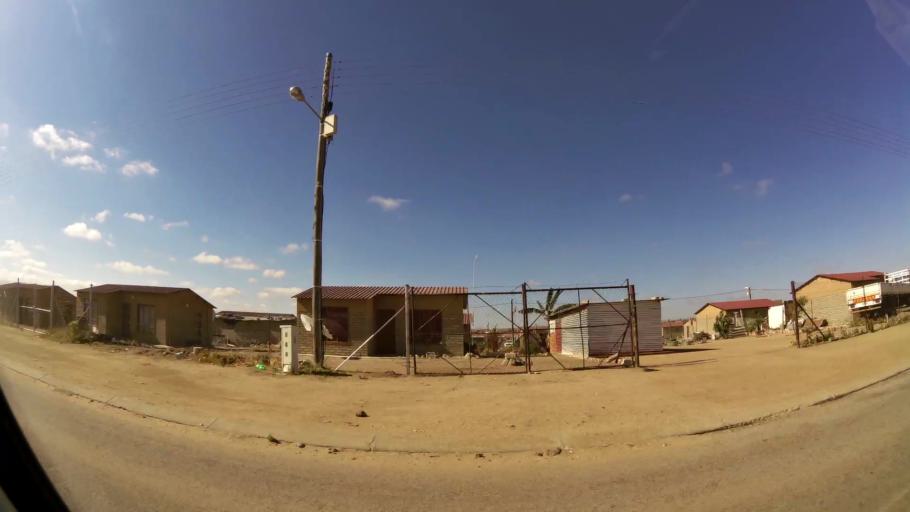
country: ZA
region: Limpopo
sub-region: Capricorn District Municipality
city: Polokwane
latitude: -23.8609
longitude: 29.3956
